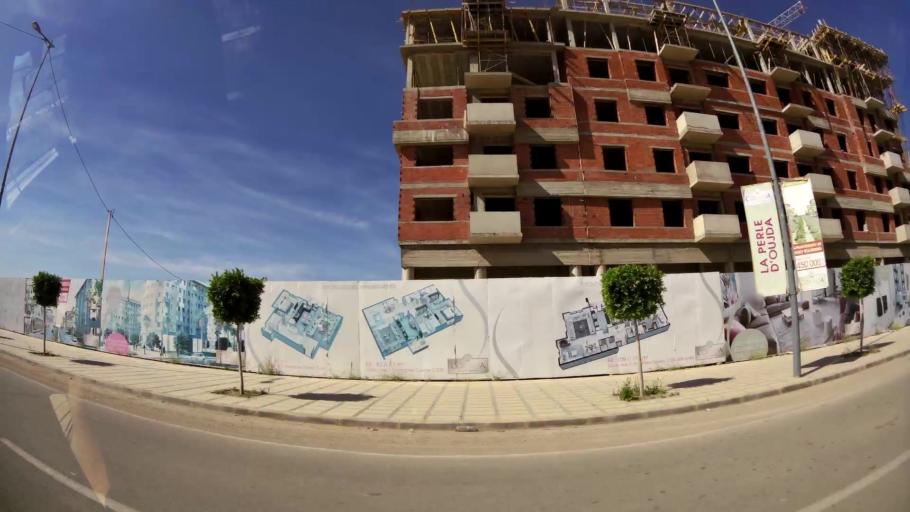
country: MA
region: Oriental
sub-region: Oujda-Angad
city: Oujda
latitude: 34.6639
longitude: -1.9147
